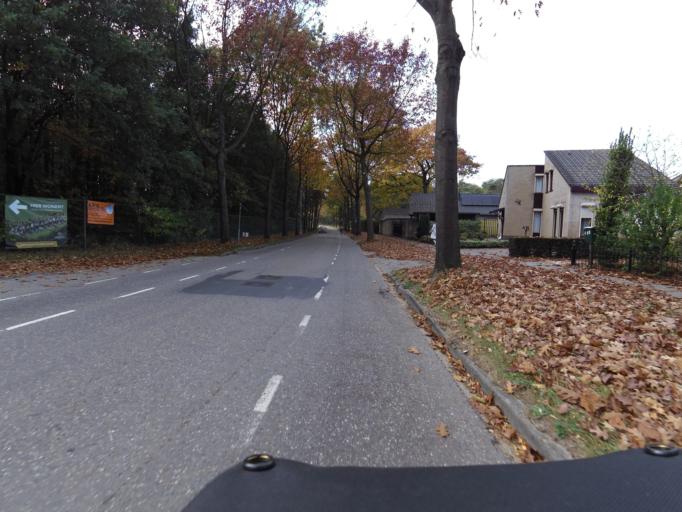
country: NL
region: Gelderland
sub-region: Gemeente Ede
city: Ede
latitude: 52.0389
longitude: 5.6868
